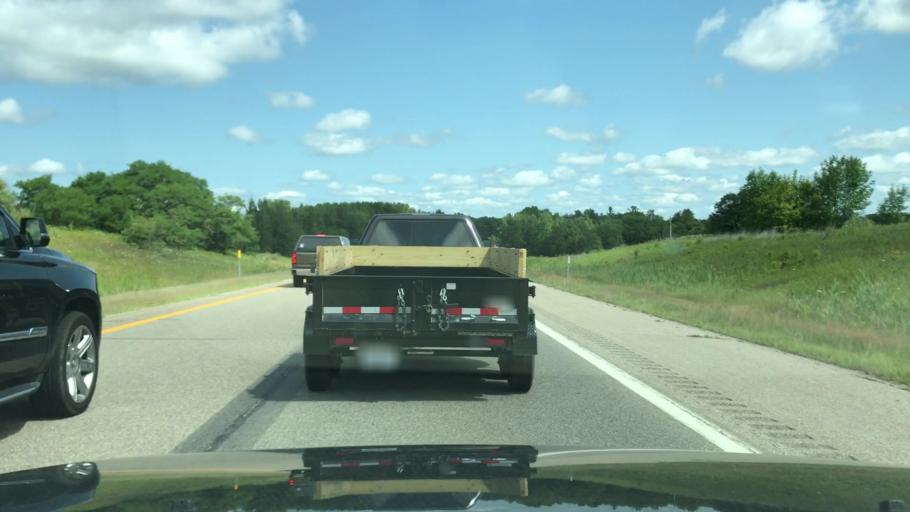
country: US
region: Michigan
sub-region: Mecosta County
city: Big Rapids
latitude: 43.7275
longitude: -85.5325
